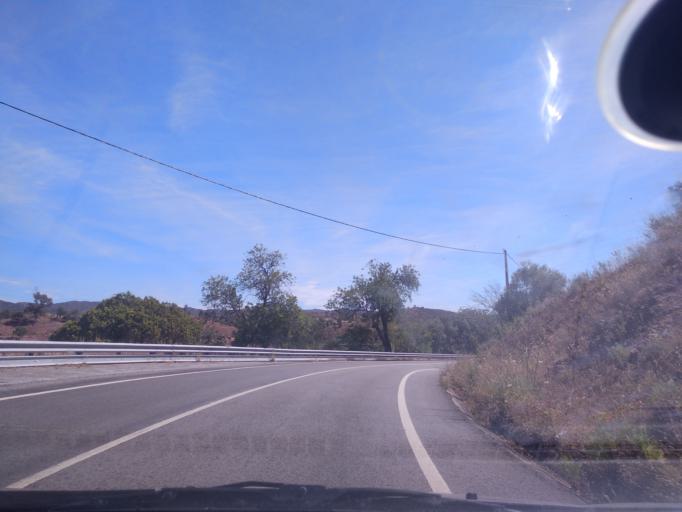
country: PT
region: Faro
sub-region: Sao Bras de Alportel
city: Sao Bras de Alportel
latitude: 37.1534
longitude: -7.8271
